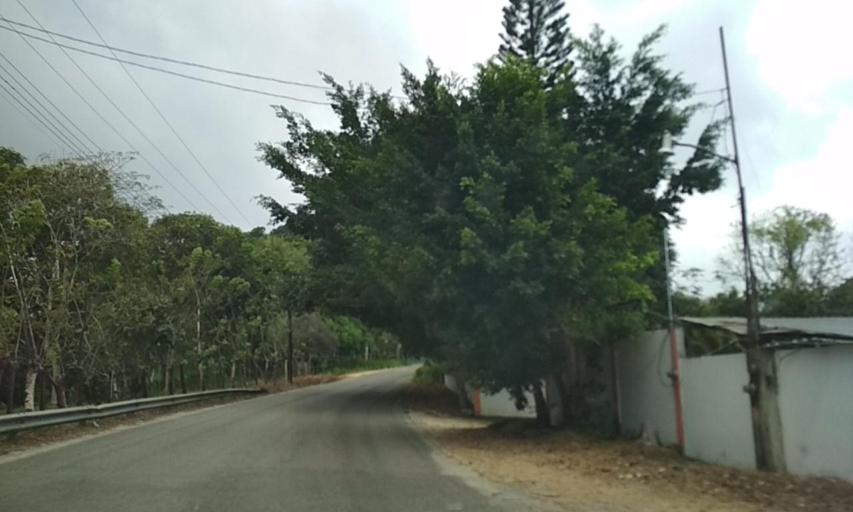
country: MX
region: Veracruz
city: Las Choapas
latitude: 17.7528
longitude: -94.1128
